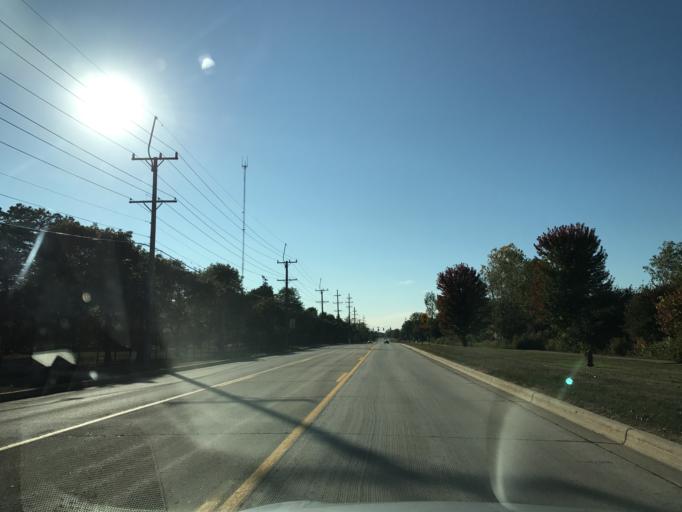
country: US
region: Michigan
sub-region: Oakland County
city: Franklin
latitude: 42.4860
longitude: -83.3006
